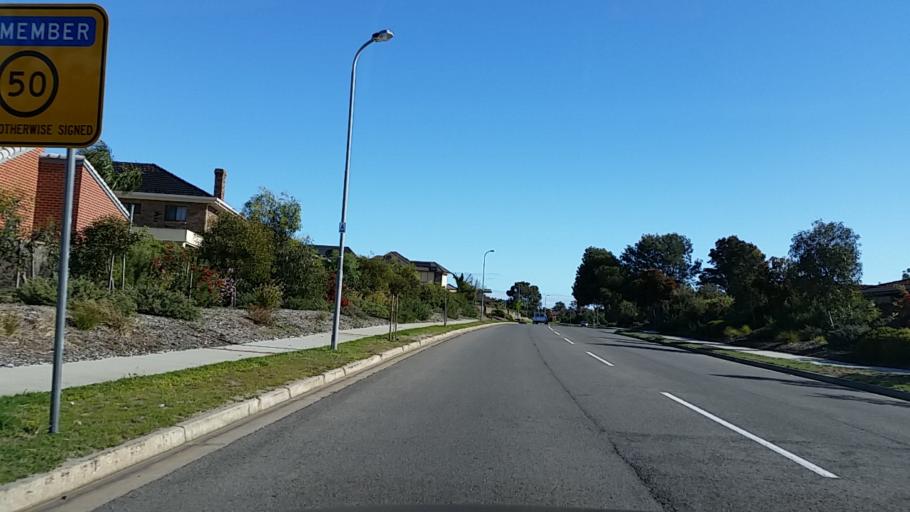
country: AU
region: South Australia
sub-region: Charles Sturt
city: West Lakes Shore
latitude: -34.8642
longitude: 138.4918
